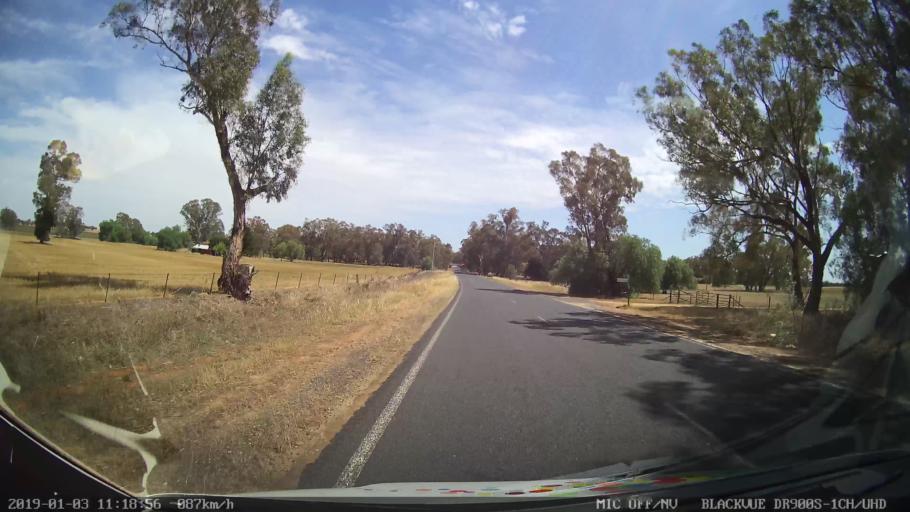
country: AU
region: New South Wales
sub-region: Young
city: Young
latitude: -34.1195
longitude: 148.2605
